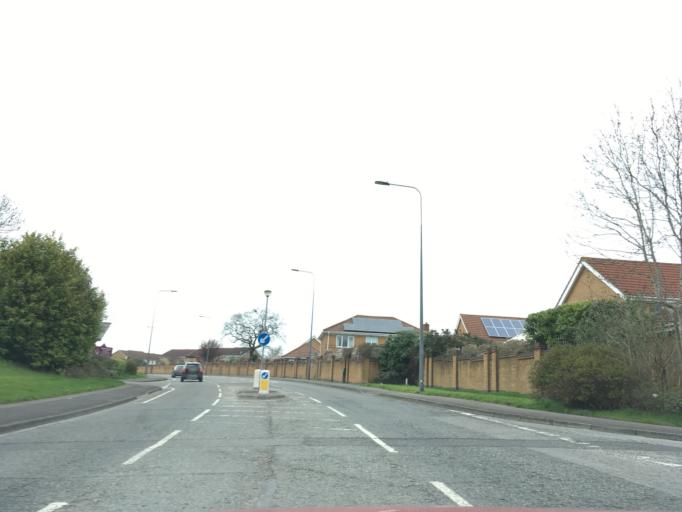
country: GB
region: England
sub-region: South Gloucestershire
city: Stoke Gifford
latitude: 51.5292
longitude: -2.5481
